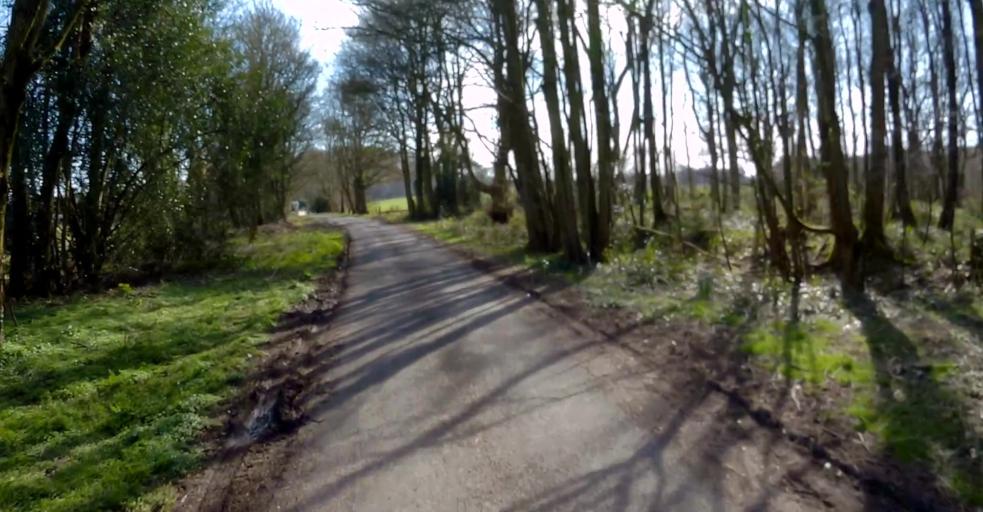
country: GB
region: England
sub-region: Hampshire
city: Four Marks
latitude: 51.1839
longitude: -1.0711
